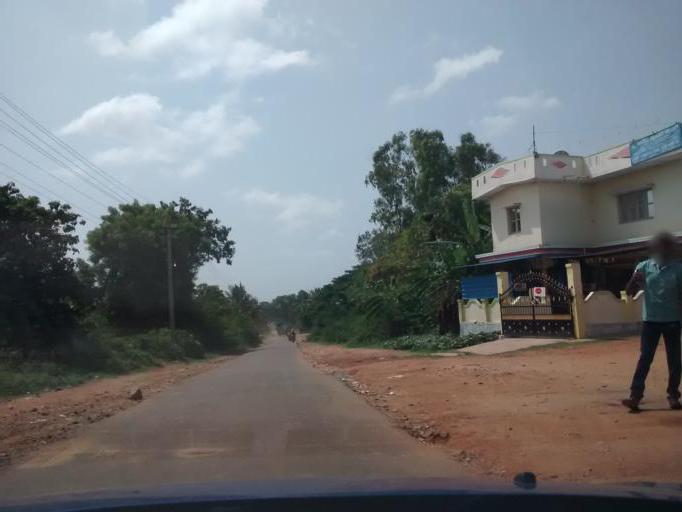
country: IN
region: Karnataka
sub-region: Hassan
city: Hole Narsipur
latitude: 12.7012
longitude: 76.1614
